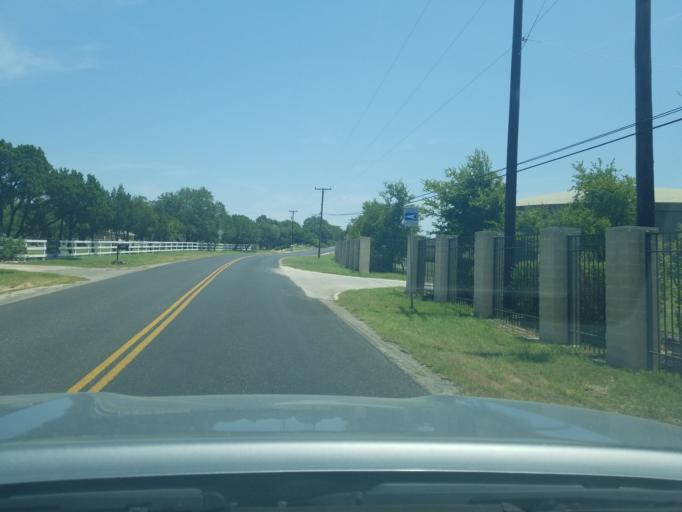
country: US
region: Texas
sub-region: Bexar County
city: Timberwood Park
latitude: 29.6667
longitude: -98.5181
